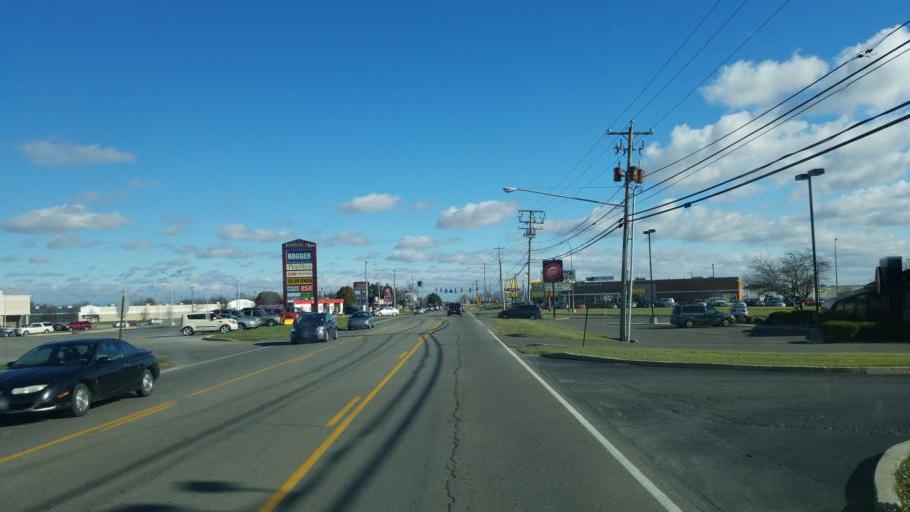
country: US
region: Ohio
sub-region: Hardin County
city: Kenton
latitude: 40.6514
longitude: -83.5927
